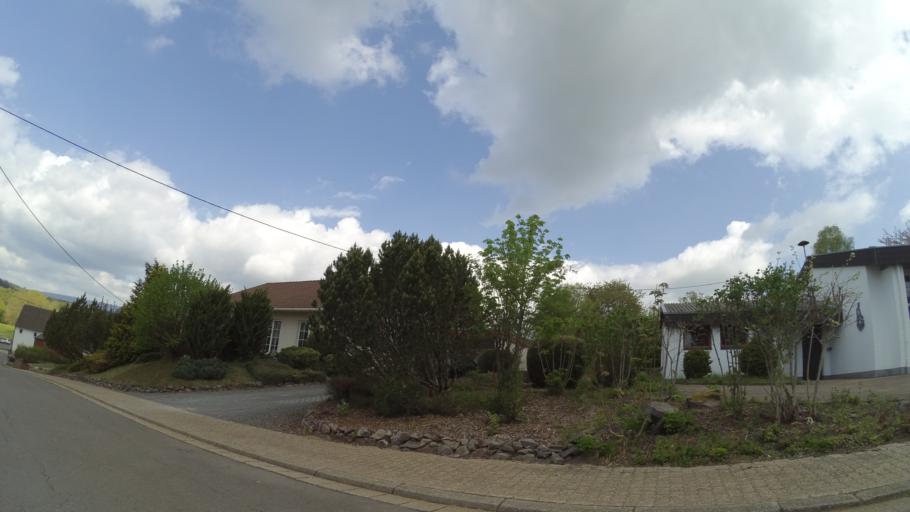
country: DE
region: Saarland
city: Wadern
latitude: 49.5242
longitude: 6.8707
